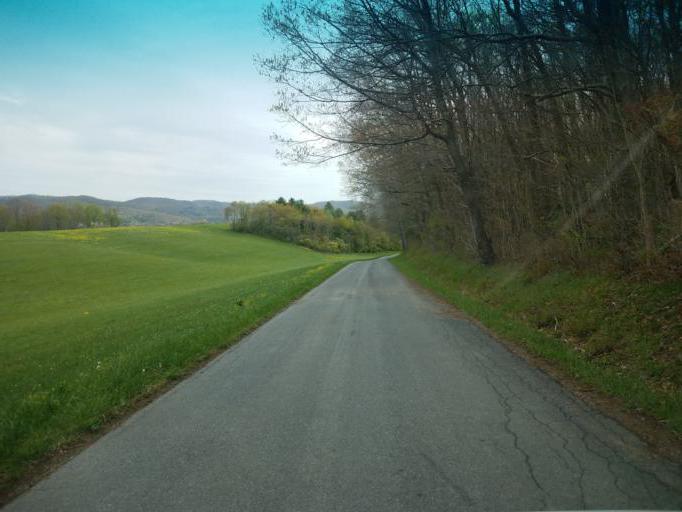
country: US
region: Virginia
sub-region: Smyth County
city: Marion
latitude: 36.7648
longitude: -81.4579
